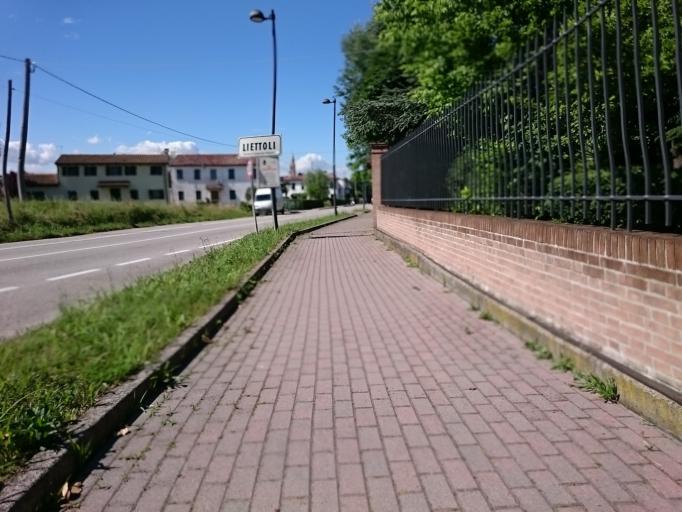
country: IT
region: Veneto
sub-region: Provincia di Venezia
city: Campolongo Maggiore Liettoli
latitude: 45.3362
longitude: 12.0213
